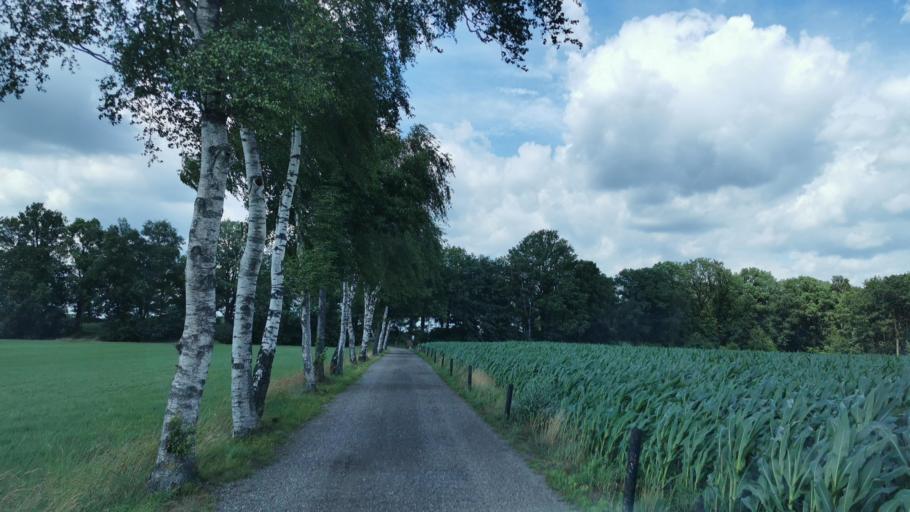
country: NL
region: Overijssel
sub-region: Gemeente Oldenzaal
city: Oldenzaal
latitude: 52.3792
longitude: 6.9112
